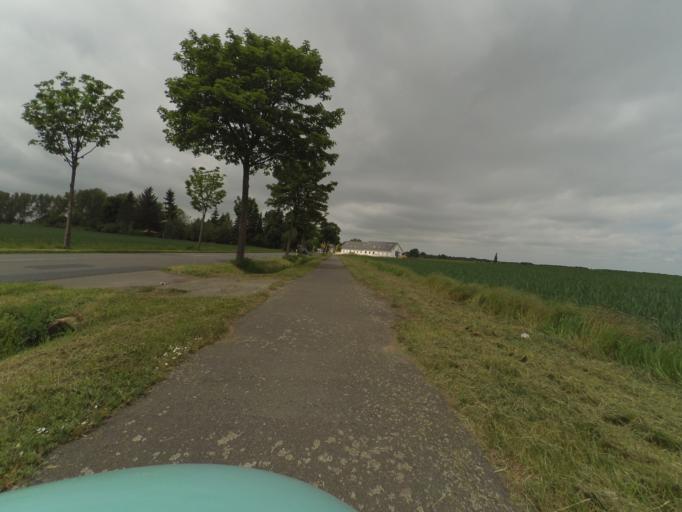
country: DE
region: Lower Saxony
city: Ribbesbuttel
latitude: 52.4294
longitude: 10.5189
